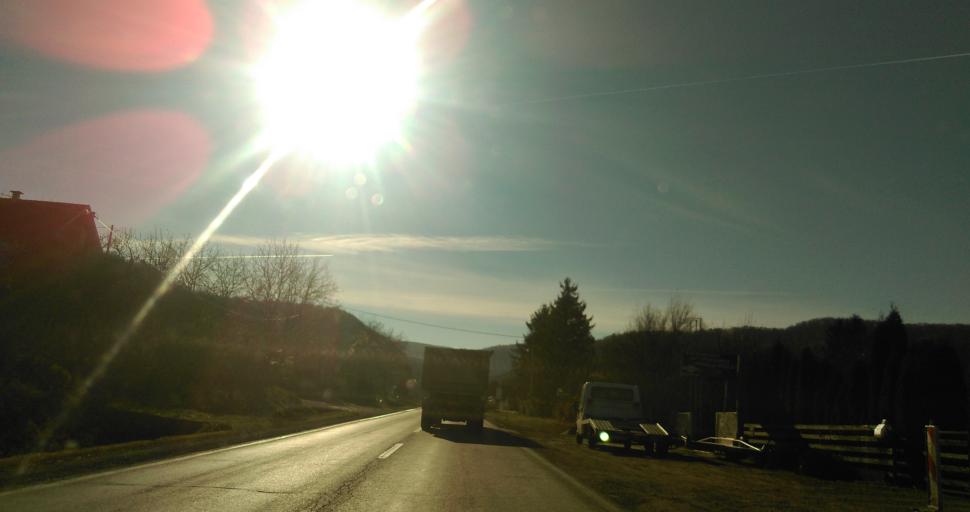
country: RS
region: Autonomna Pokrajina Vojvodina
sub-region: Juznobacki Okrug
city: Novi Sad
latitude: 45.1950
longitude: 19.8411
